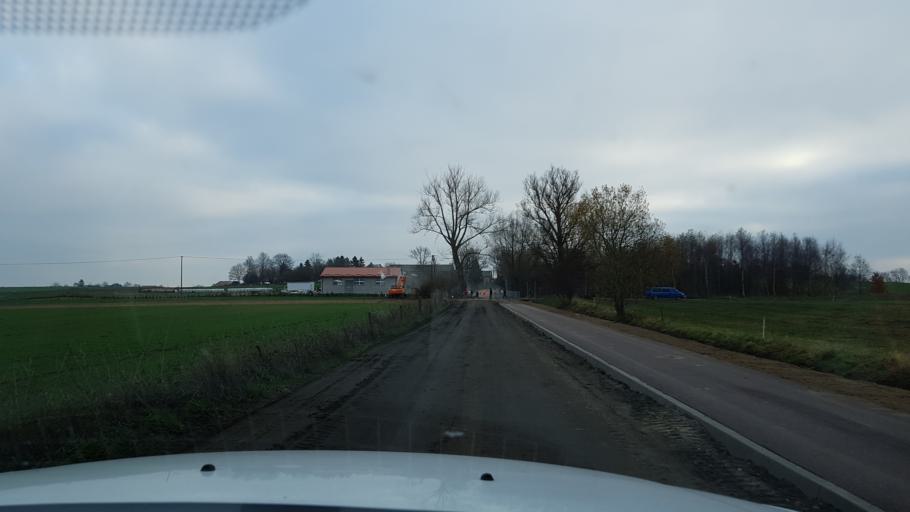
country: PL
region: West Pomeranian Voivodeship
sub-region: Powiat kolobrzeski
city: Grzybowo
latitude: 54.1228
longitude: 15.5205
